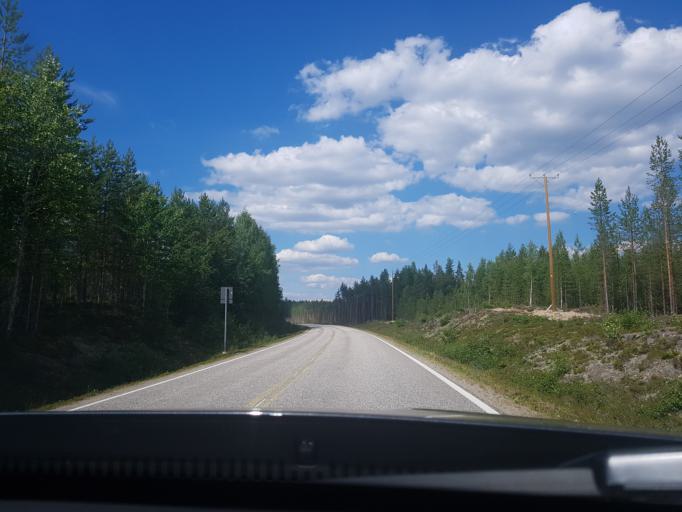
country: FI
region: Kainuu
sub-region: Kehys-Kainuu
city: Kuhmo
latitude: 64.2341
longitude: 29.8187
